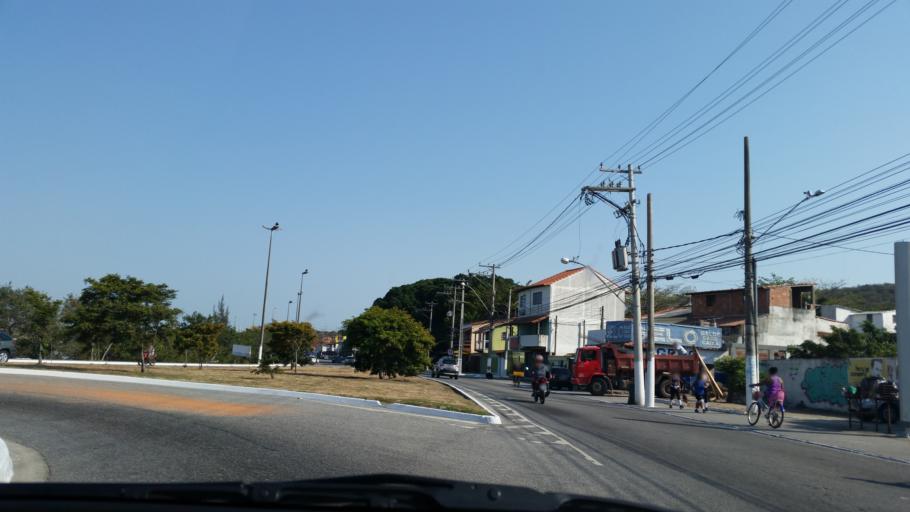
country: BR
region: Rio de Janeiro
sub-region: Cabo Frio
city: Cabo Frio
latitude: -22.8725
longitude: -42.0235
